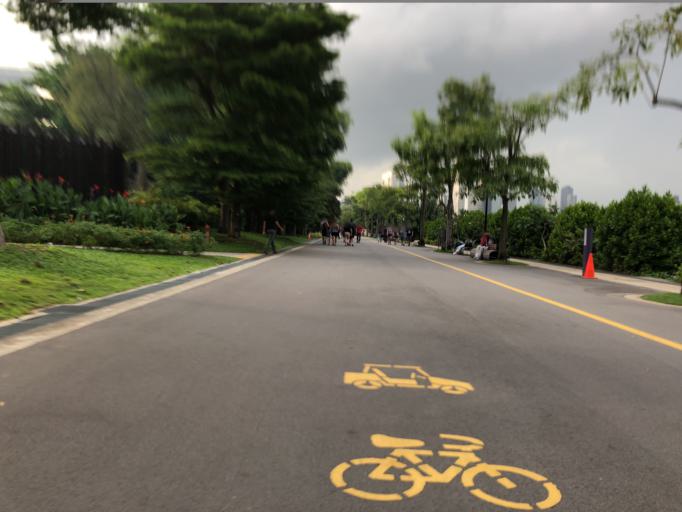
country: SG
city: Singapore
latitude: 1.2825
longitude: 103.8690
